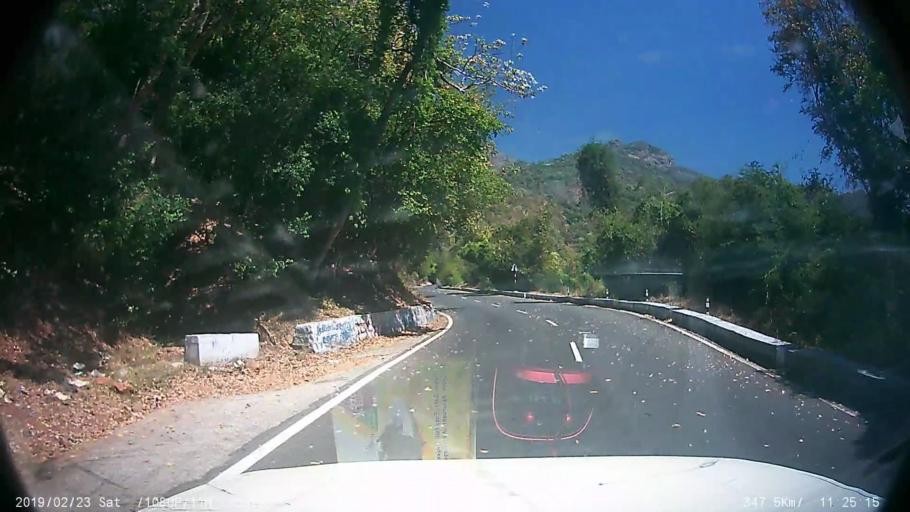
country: IN
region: Tamil Nadu
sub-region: Coimbatore
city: Mettupalayam
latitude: 11.3410
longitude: 76.8731
